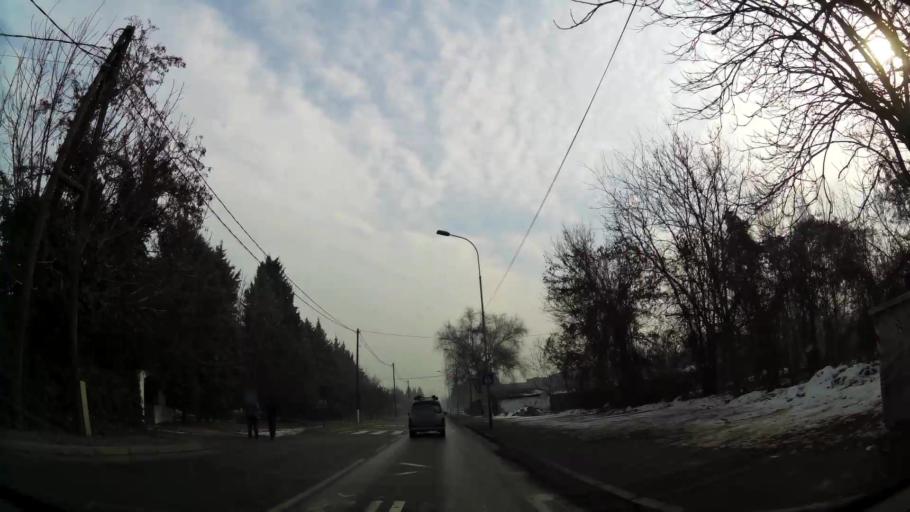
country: MK
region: Cair
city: Cair
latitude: 42.0025
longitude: 21.4806
